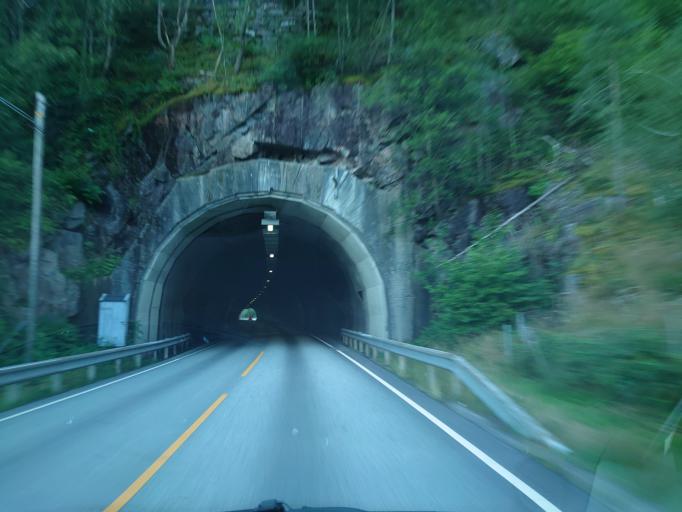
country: NO
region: Hordaland
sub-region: Osteroy
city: Lonevag
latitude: 60.6983
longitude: 5.5733
